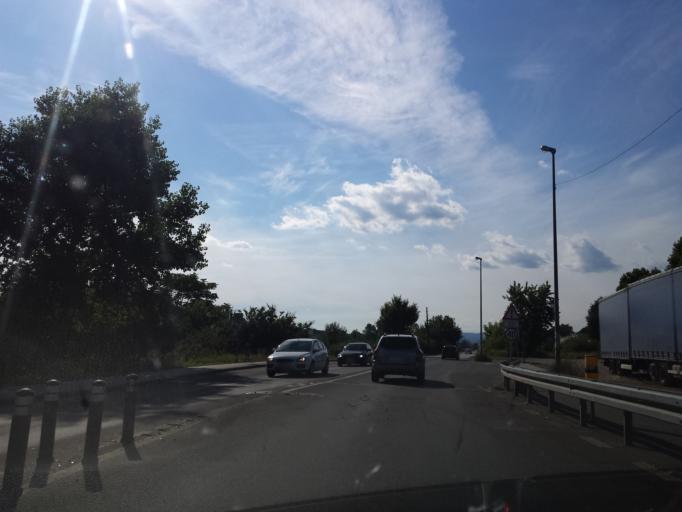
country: HR
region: Zagrebacka
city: Micevec
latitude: 45.7760
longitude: 16.0598
